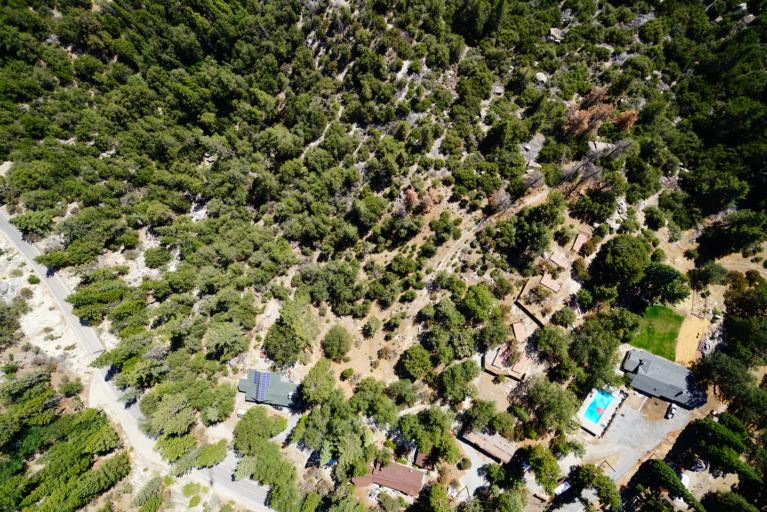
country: US
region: California
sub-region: Riverside County
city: Idyllwild-Pine Cove
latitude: 33.7818
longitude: -116.7502
